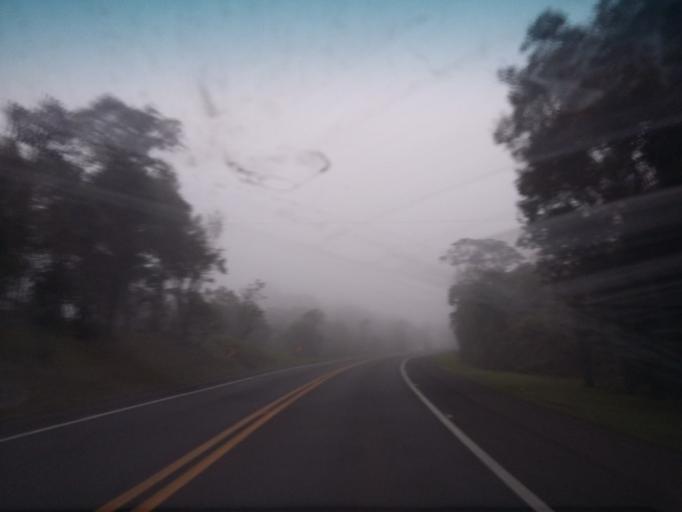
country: BR
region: Santa Catarina
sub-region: Correia Pinto
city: Correia Pinto
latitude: -27.4353
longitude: -50.4074
